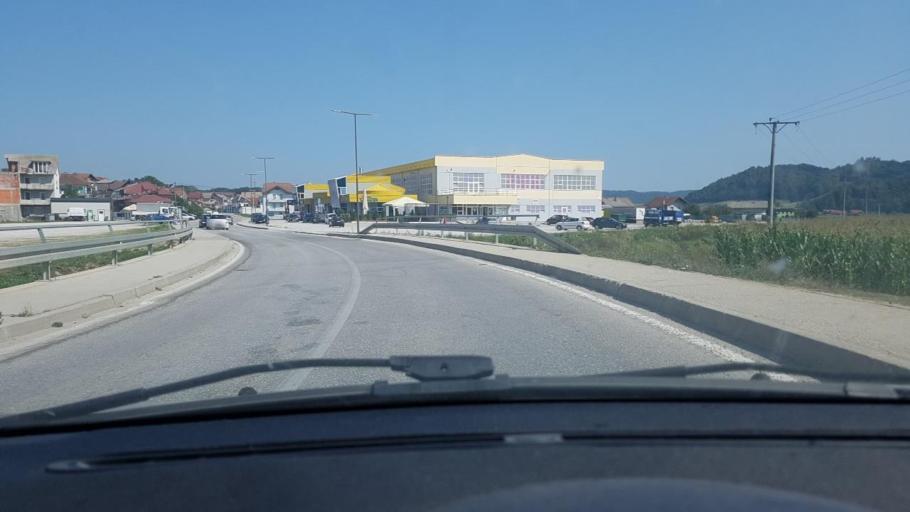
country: BA
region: Federation of Bosnia and Herzegovina
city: Velika Kladusa
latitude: 45.1832
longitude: 15.8132
